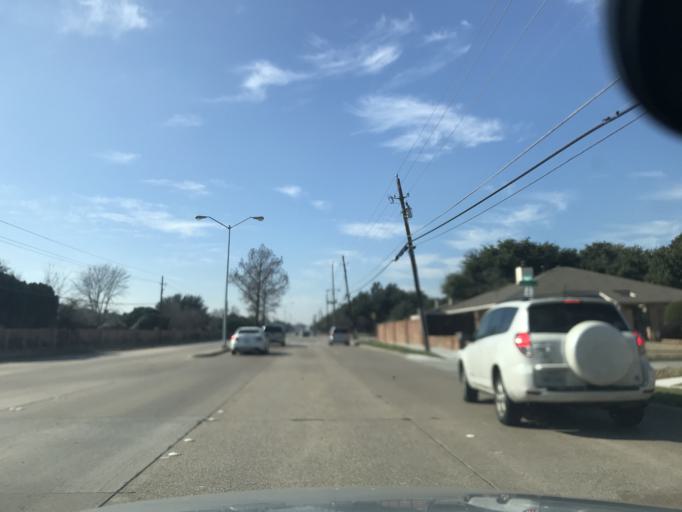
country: US
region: Texas
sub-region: Collin County
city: Plano
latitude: 33.0411
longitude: -96.7286
